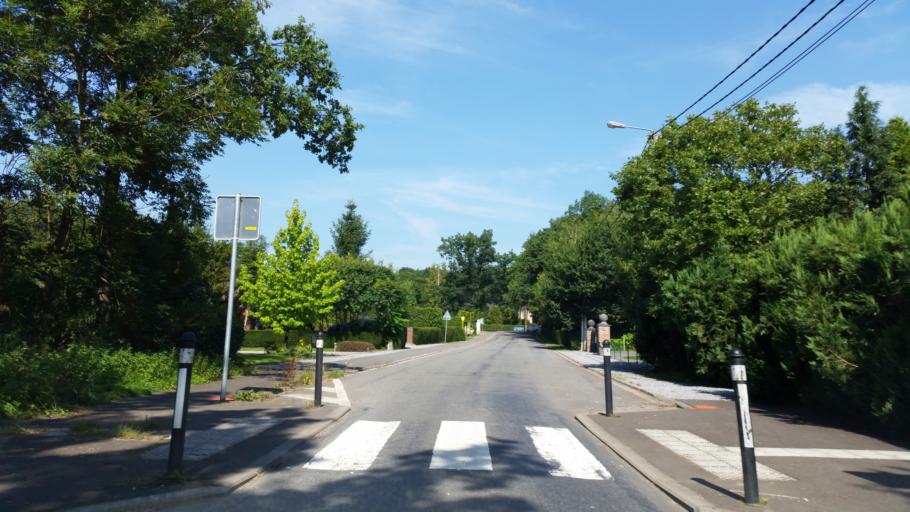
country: BE
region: Wallonia
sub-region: Province du Luxembourg
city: Durbuy
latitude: 50.3429
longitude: 5.4716
